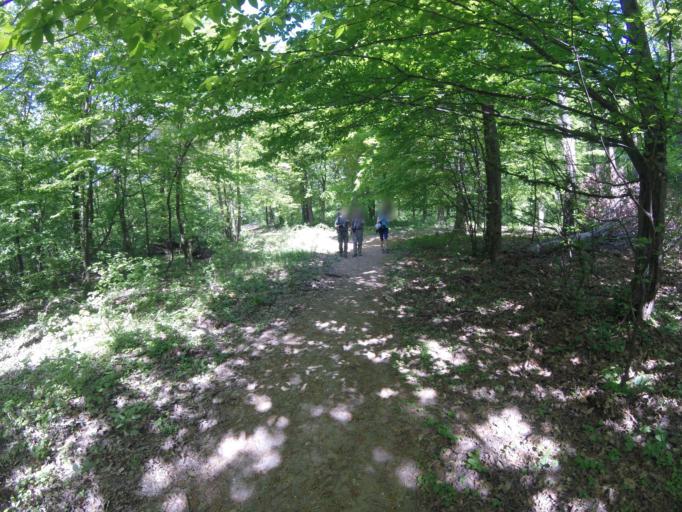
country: HU
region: Pest
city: Nagymaros
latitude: 47.7930
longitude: 18.9255
